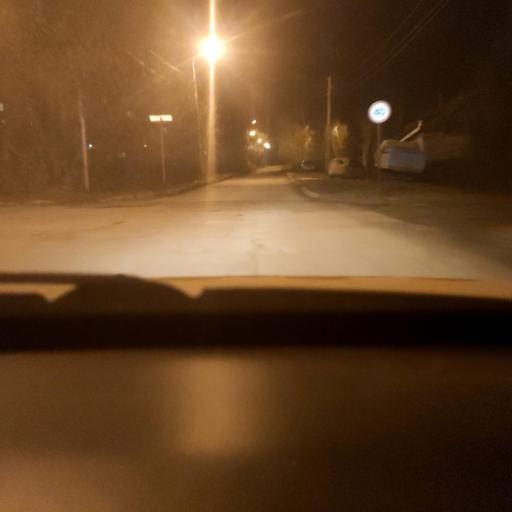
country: RU
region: Perm
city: Polazna
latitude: 58.1364
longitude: 56.3881
